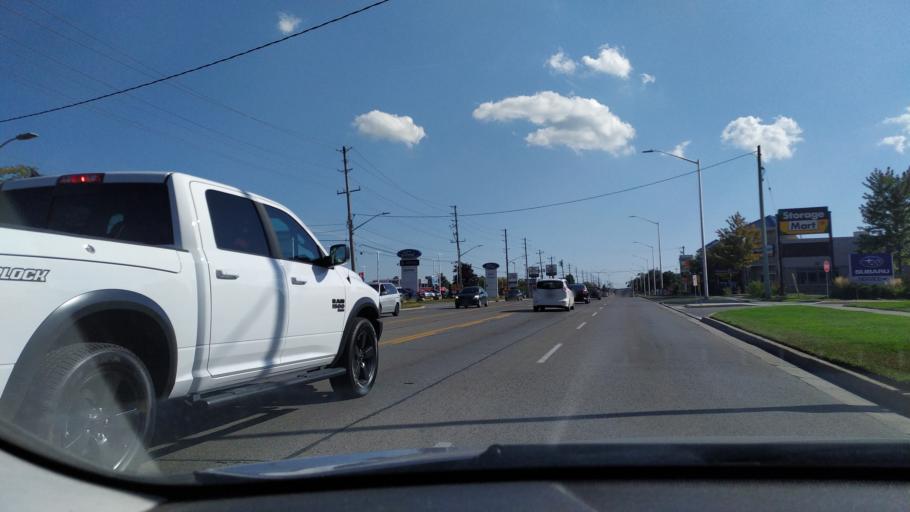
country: CA
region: Ontario
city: London
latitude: 42.9501
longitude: -81.2590
